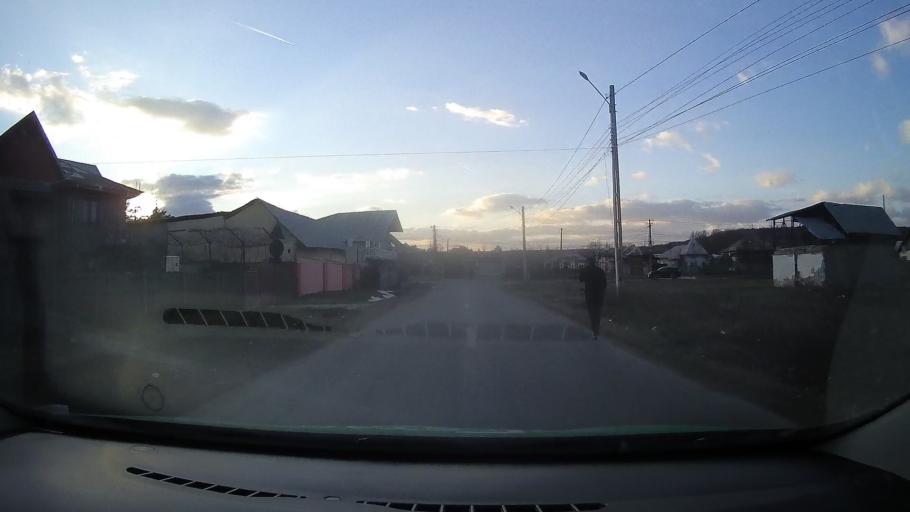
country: RO
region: Dambovita
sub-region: Comuna Gura Ocnitei
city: Gura Ocnitei
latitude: 44.9390
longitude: 25.5803
